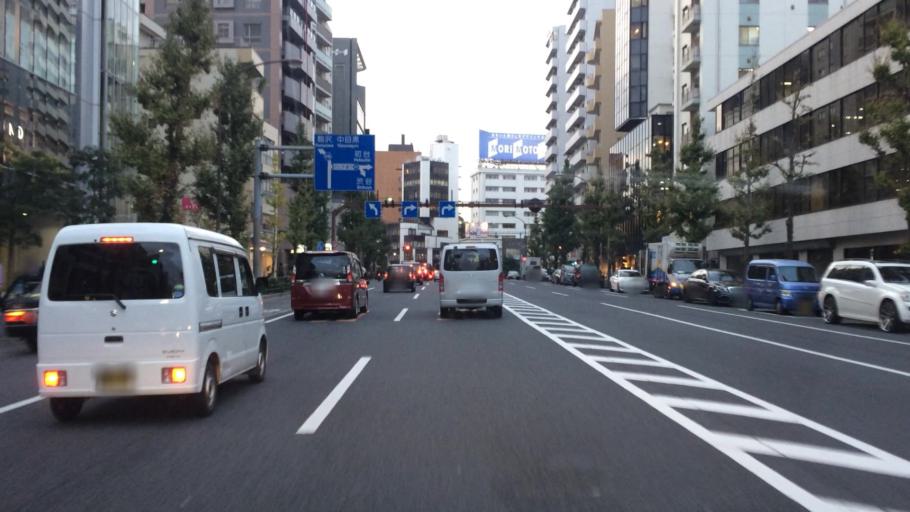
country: JP
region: Tokyo
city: Tokyo
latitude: 35.6465
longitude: 139.7043
